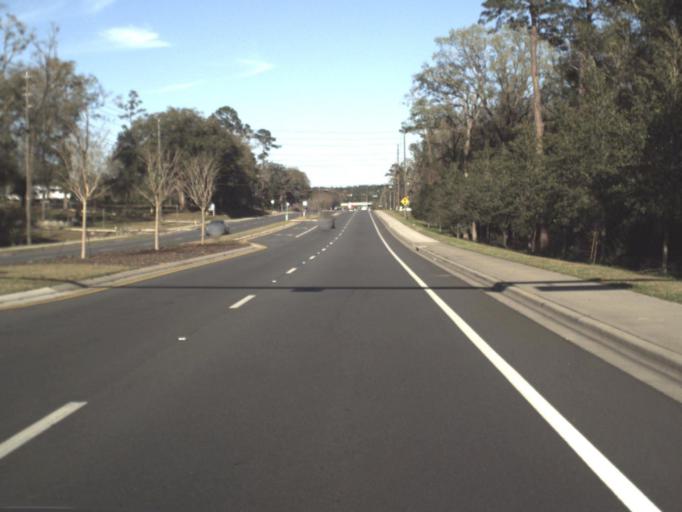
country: US
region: Florida
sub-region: Leon County
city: Tallahassee
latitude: 30.4802
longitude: -84.1718
